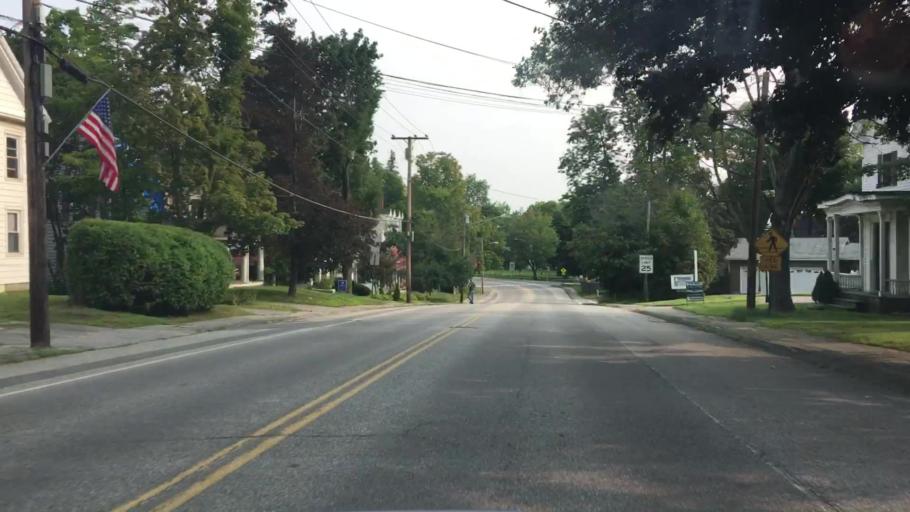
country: US
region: Maine
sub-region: Kennebec County
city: Gardiner
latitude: 44.2251
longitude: -69.7768
